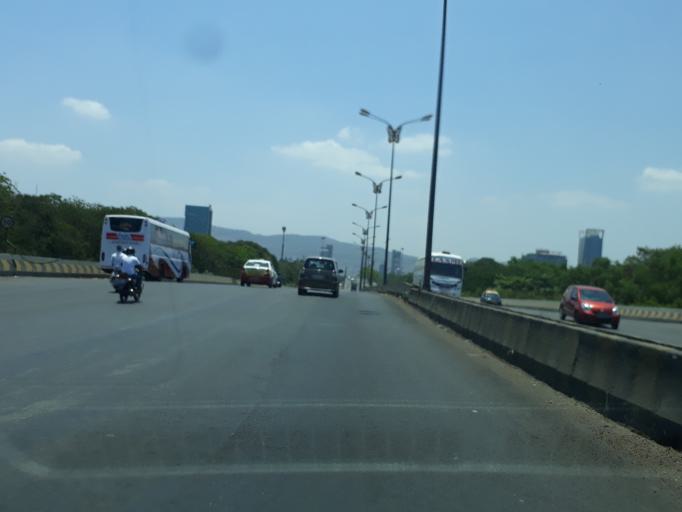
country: IN
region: Maharashtra
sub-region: Thane
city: Navi Mumbai
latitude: 19.0694
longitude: 72.9900
